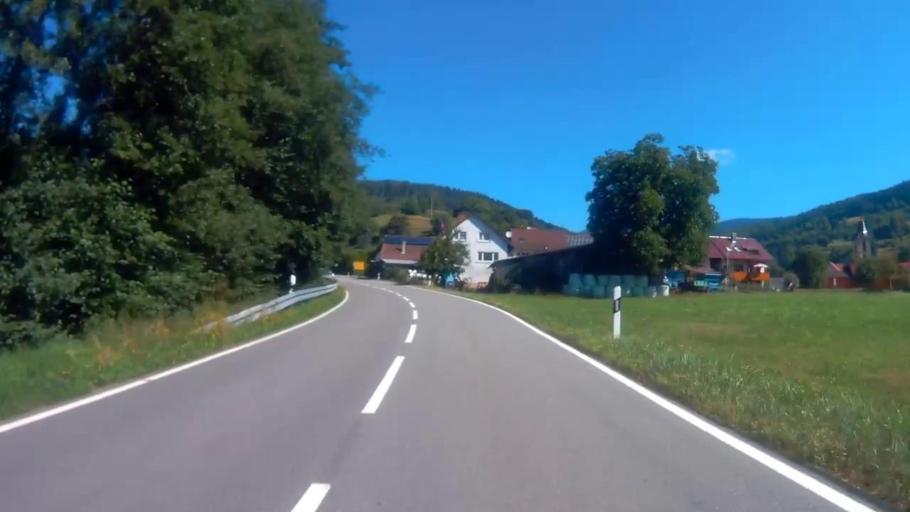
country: DE
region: Baden-Wuerttemberg
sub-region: Freiburg Region
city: Bollen
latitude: 47.7467
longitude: 7.7678
